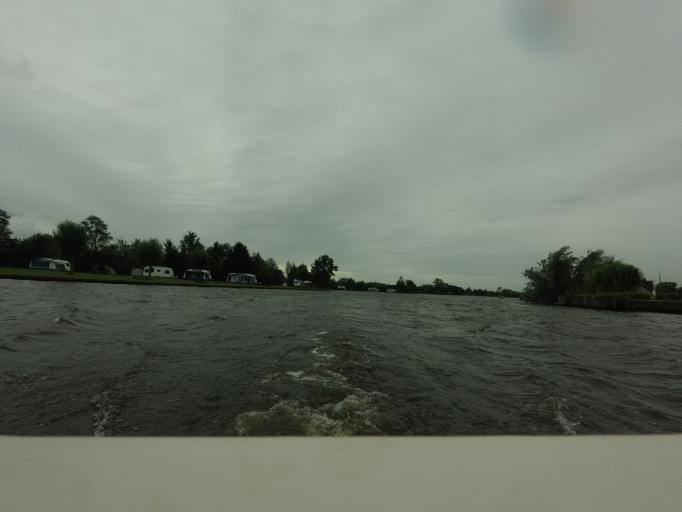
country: NL
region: Friesland
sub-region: Gemeente Boarnsterhim
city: Warten
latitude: 53.1283
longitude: 5.9387
